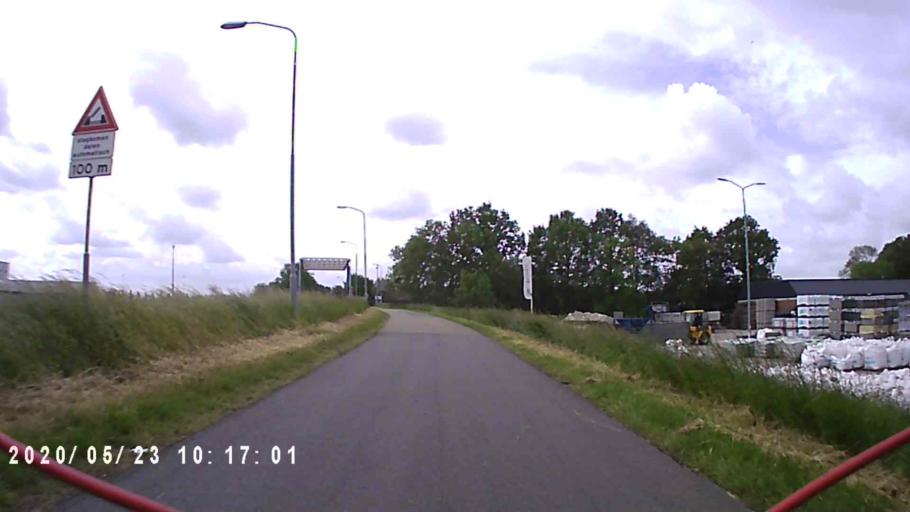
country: NL
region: Groningen
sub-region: Gemeente Appingedam
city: Appingedam
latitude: 53.3076
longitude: 6.8541
